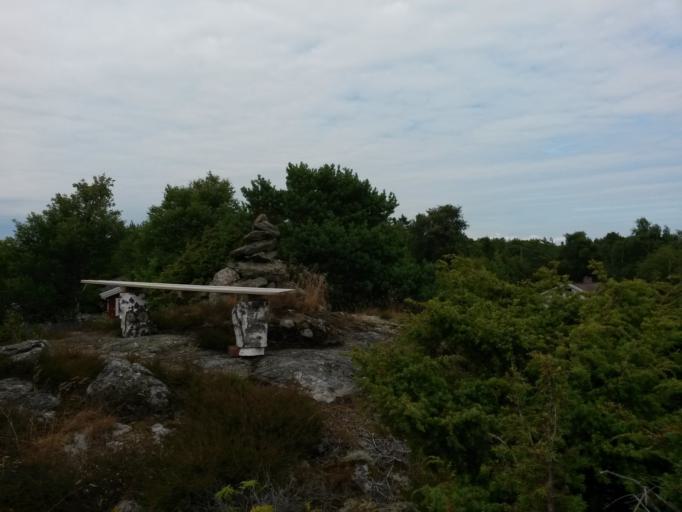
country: SE
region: Vaestra Goetaland
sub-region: Tjorns Kommun
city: Hoviksnas
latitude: 57.9605
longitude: 11.7724
